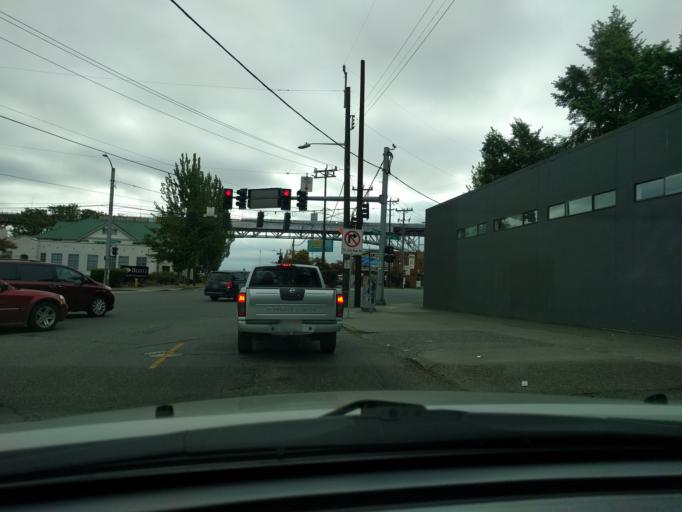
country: US
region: Washington
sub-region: King County
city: Seattle
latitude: 47.6469
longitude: -122.3519
